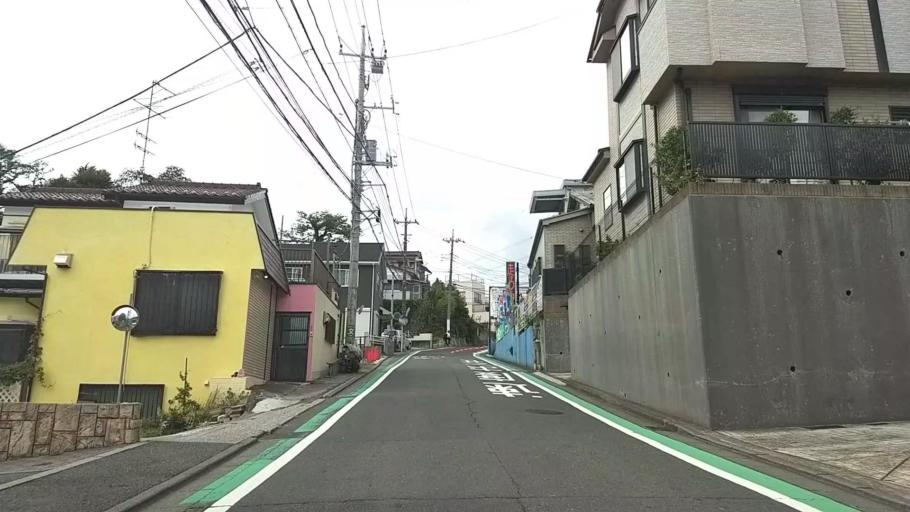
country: JP
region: Kanagawa
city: Yokohama
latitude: 35.4101
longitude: 139.5539
